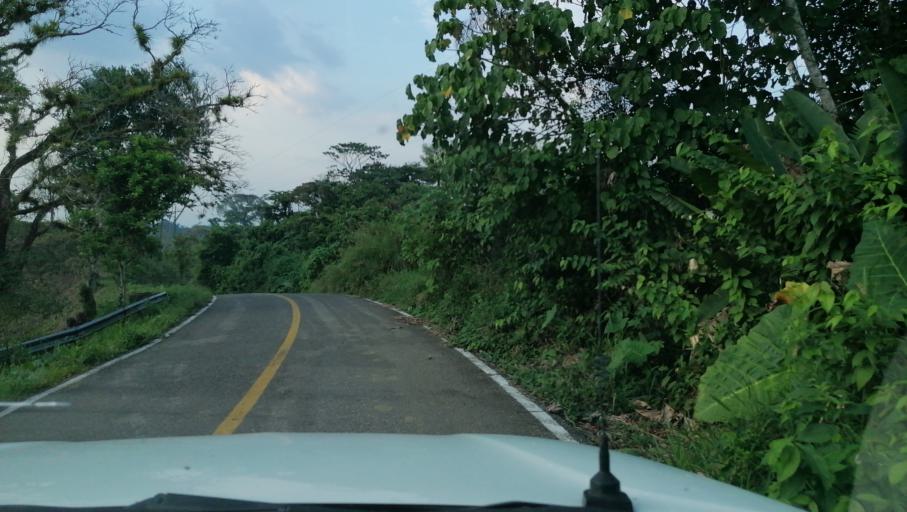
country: MX
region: Chiapas
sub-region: Juarez
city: El Triunfo 1ra. Seccion (Cardona)
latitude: 17.4978
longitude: -93.2456
